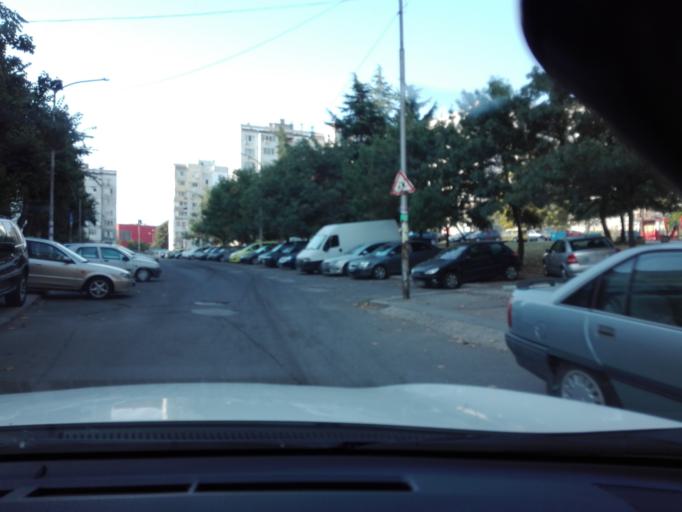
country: BG
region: Burgas
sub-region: Obshtina Burgas
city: Burgas
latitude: 42.4638
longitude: 27.4155
